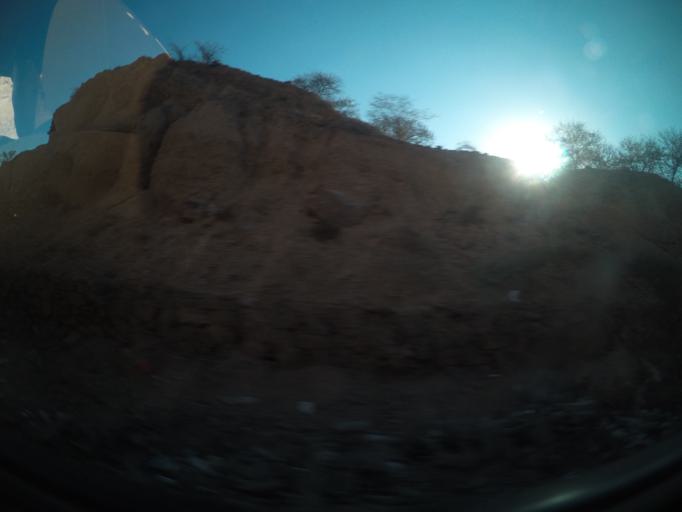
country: YE
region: Ad Dali'
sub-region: Ad Dhale'e
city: Dhalie
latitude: 13.6727
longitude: 44.7655
